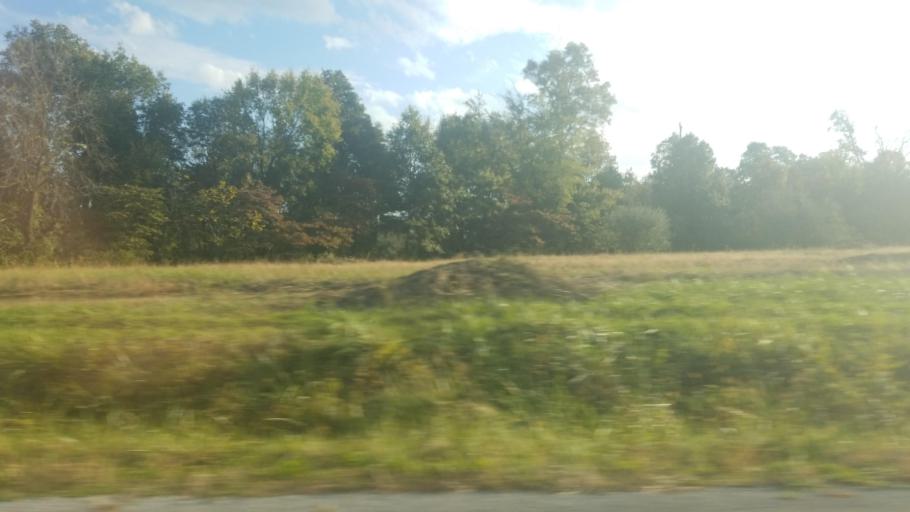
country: US
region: Illinois
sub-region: Saline County
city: Carrier Mills
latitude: 37.8051
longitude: -88.6989
